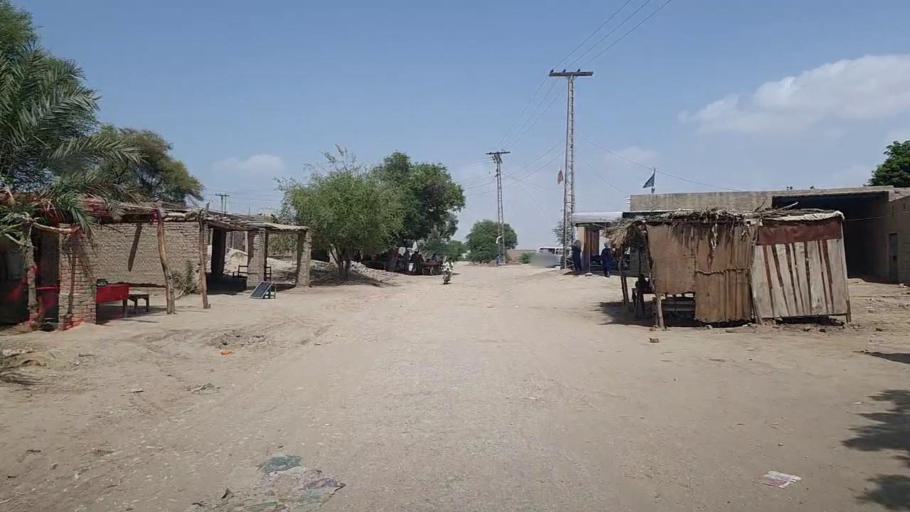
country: PK
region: Sindh
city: Pad Idan
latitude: 26.7852
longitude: 68.3393
